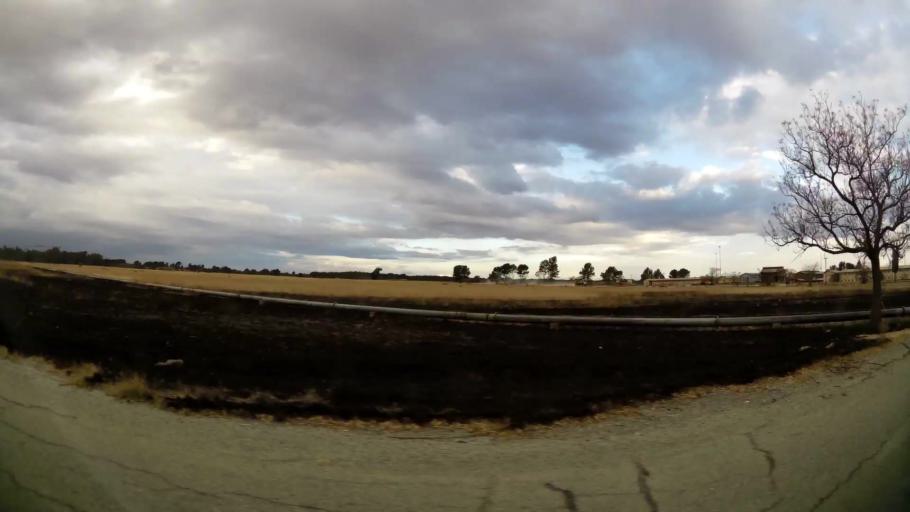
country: ZA
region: Orange Free State
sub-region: Lejweleputswa District Municipality
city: Welkom
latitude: -27.9667
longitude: 26.7031
